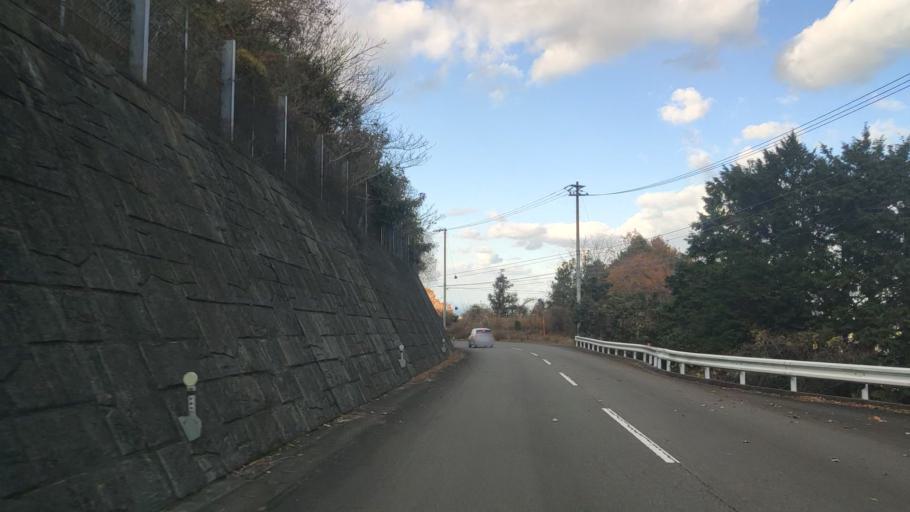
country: JP
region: Ehime
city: Saijo
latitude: 33.8826
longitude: 133.1327
